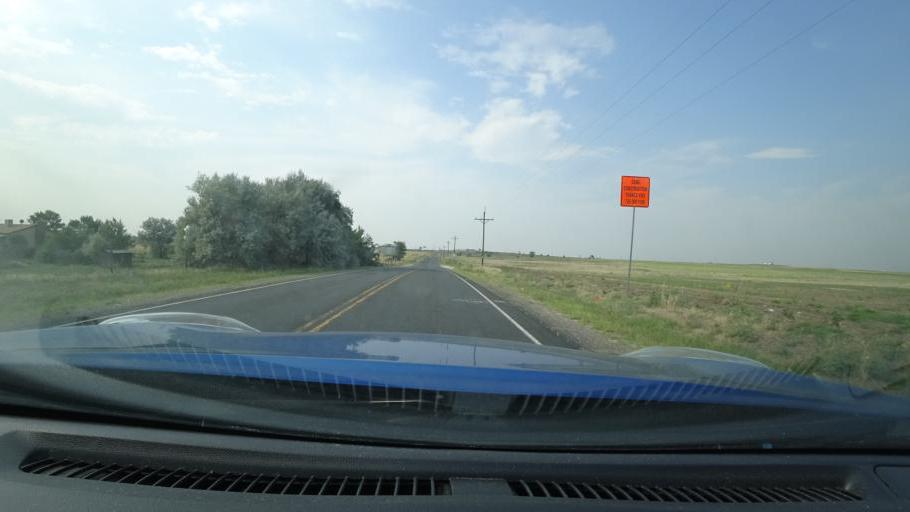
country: US
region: Colorado
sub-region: Adams County
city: Aurora
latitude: 39.7320
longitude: -104.7351
